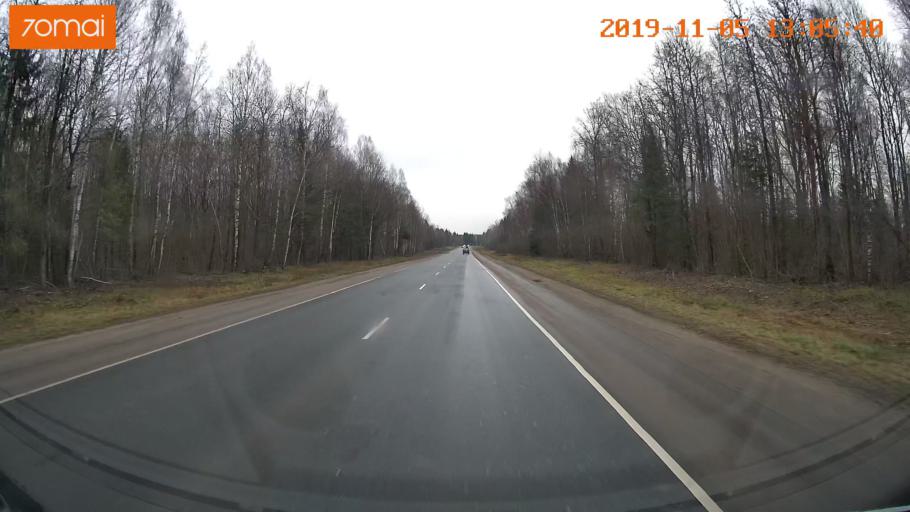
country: RU
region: Ivanovo
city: Kitovo
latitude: 56.8811
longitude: 41.2477
